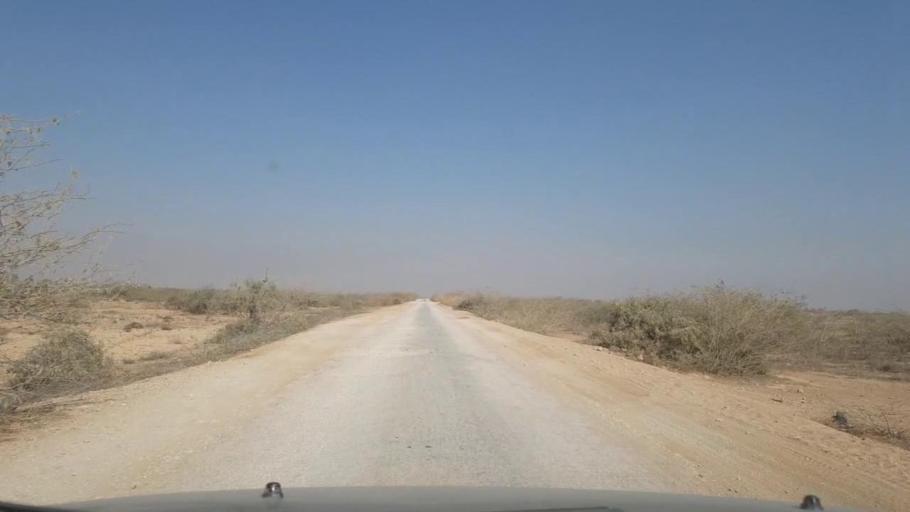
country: PK
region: Sindh
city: Thatta
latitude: 24.9189
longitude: 67.9367
